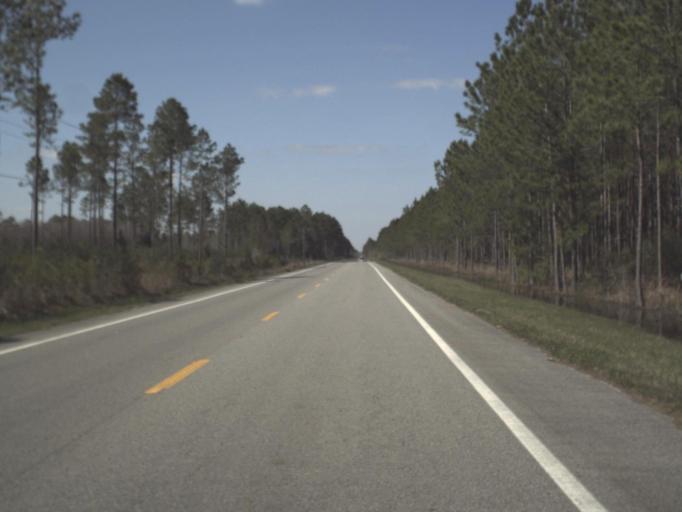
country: US
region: Florida
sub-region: Gulf County
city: Wewahitchka
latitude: 30.0059
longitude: -85.1741
